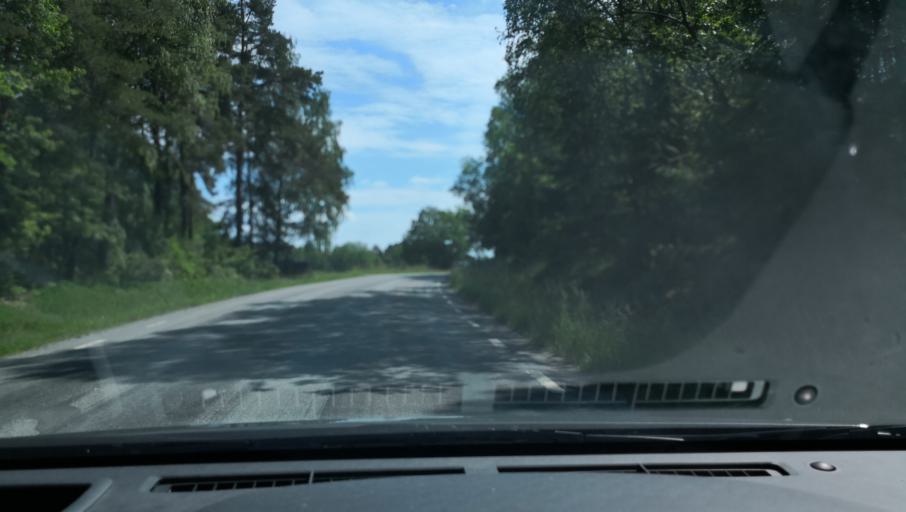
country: SE
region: Uppsala
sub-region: Habo Kommun
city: Balsta
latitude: 59.6552
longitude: 17.4567
